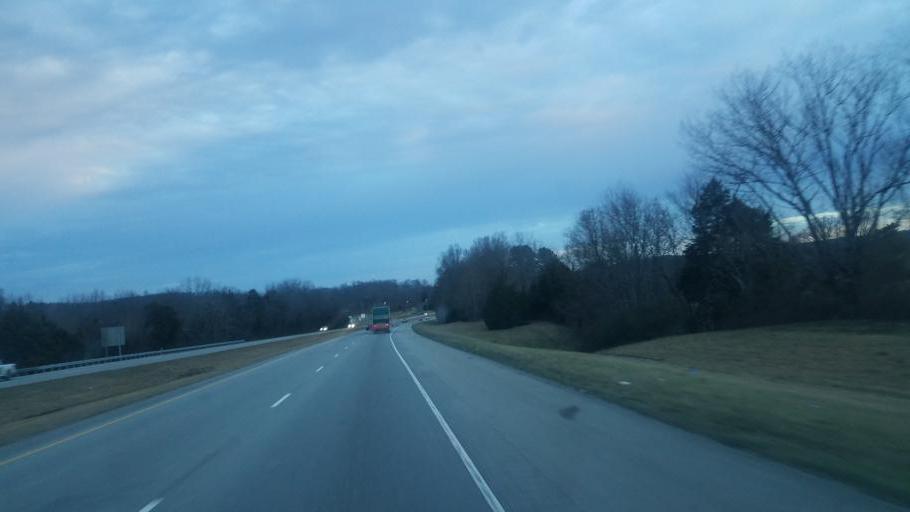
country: US
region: Tennessee
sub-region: White County
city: Sparta
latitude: 35.9530
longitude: -85.4846
